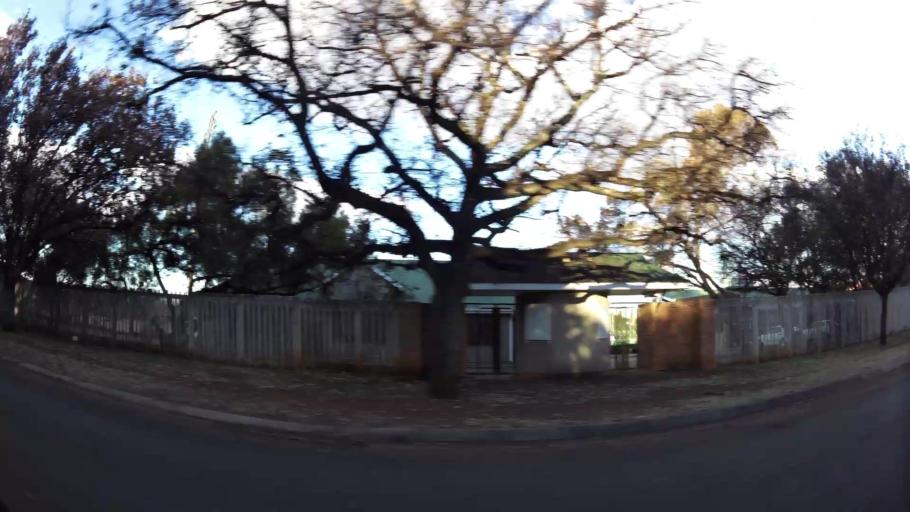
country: ZA
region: North-West
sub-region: Dr Kenneth Kaunda District Municipality
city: Potchefstroom
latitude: -26.6831
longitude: 27.0957
